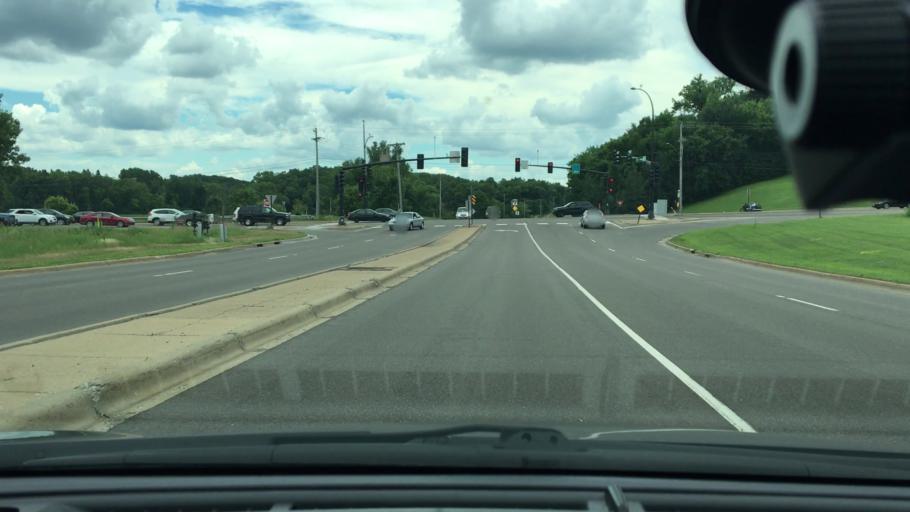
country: US
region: Minnesota
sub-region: Hennepin County
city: Plymouth
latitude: 45.0297
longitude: -93.4454
